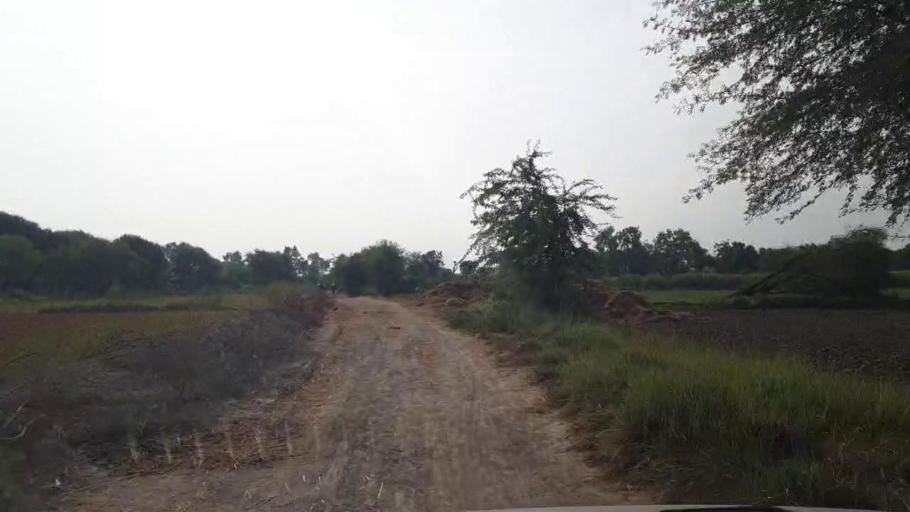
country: PK
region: Sindh
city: Rajo Khanani
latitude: 24.9062
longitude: 68.9209
